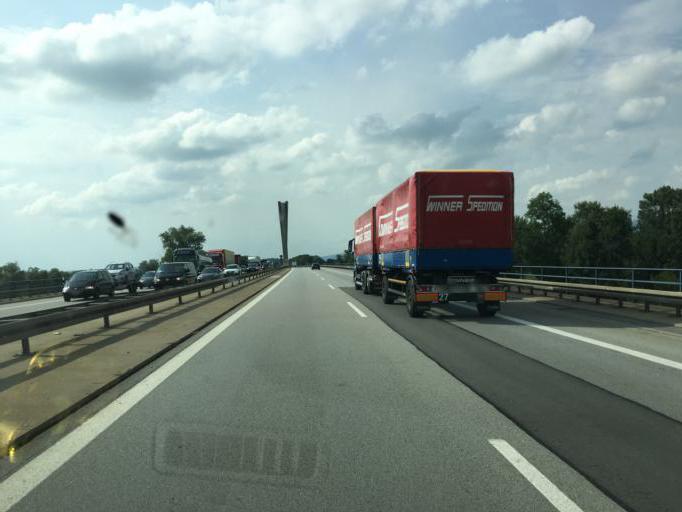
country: DE
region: Bavaria
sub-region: Lower Bavaria
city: Metten
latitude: 48.8417
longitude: 12.8966
